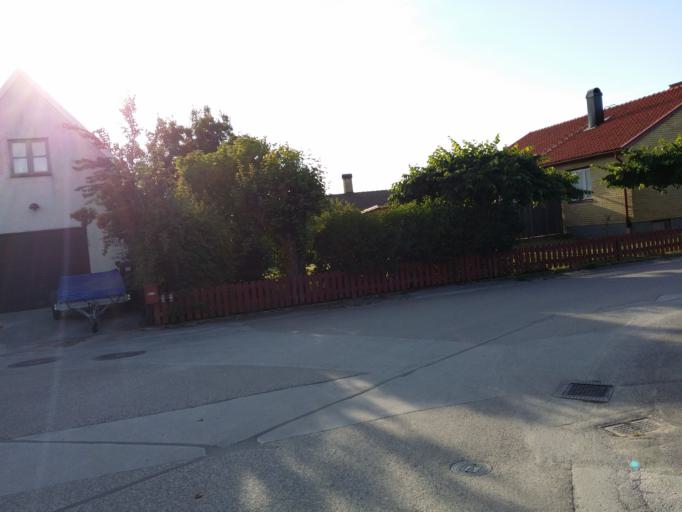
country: SE
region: Gotland
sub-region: Gotland
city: Visby
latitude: 57.6342
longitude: 18.3201
